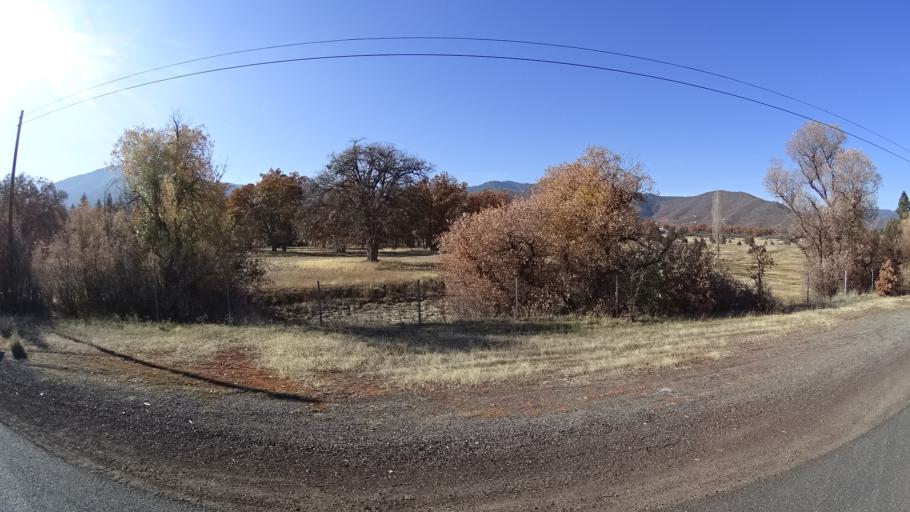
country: US
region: California
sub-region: Siskiyou County
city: Yreka
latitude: 41.6690
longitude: -122.6135
